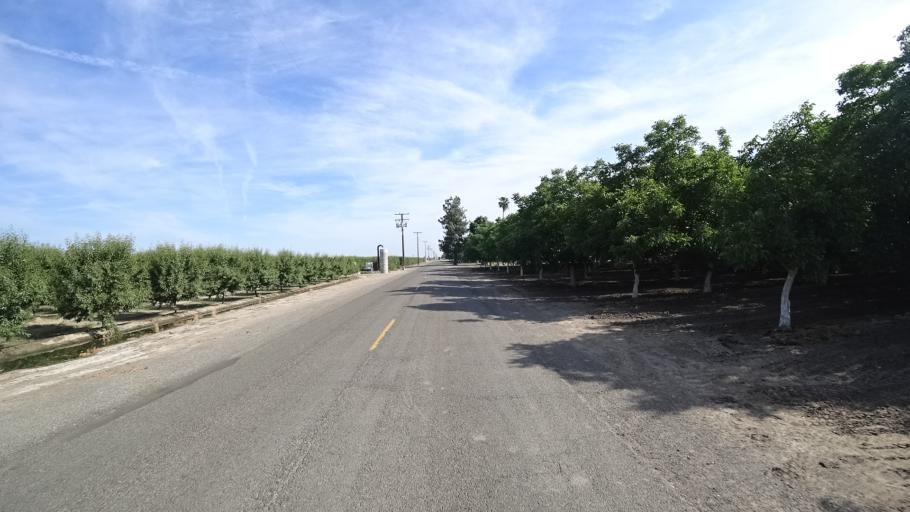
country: US
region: California
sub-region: Tulare County
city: Goshen
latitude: 36.3325
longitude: -119.4931
